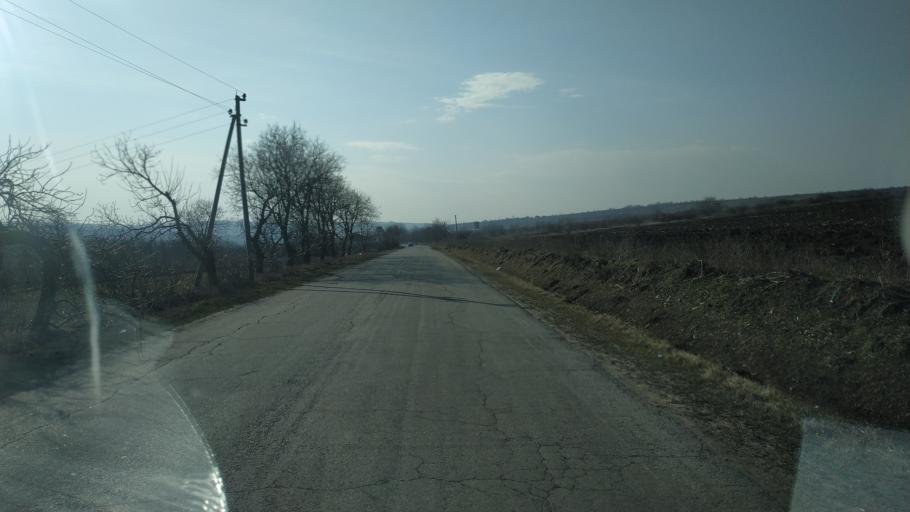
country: MD
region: Chisinau
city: Singera
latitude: 46.8456
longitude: 29.0247
